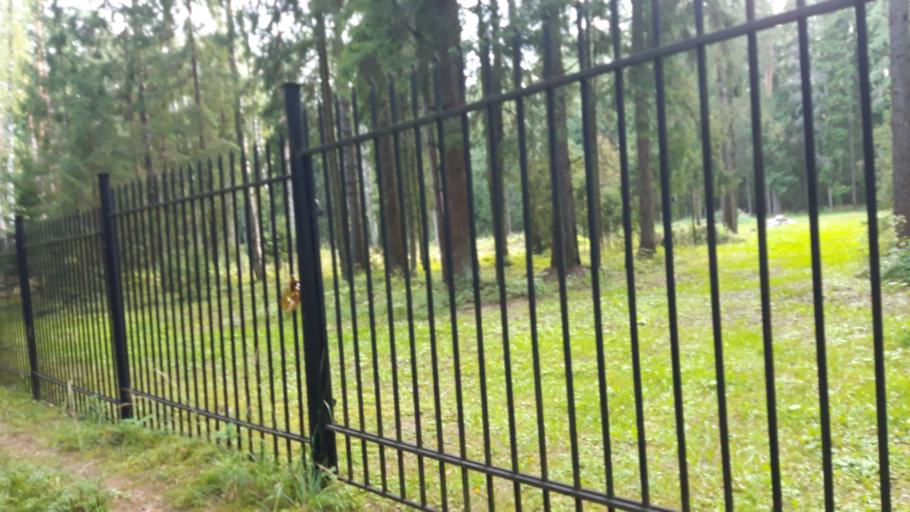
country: RU
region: Tverskaya
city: Konakovo
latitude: 56.6924
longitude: 36.7211
